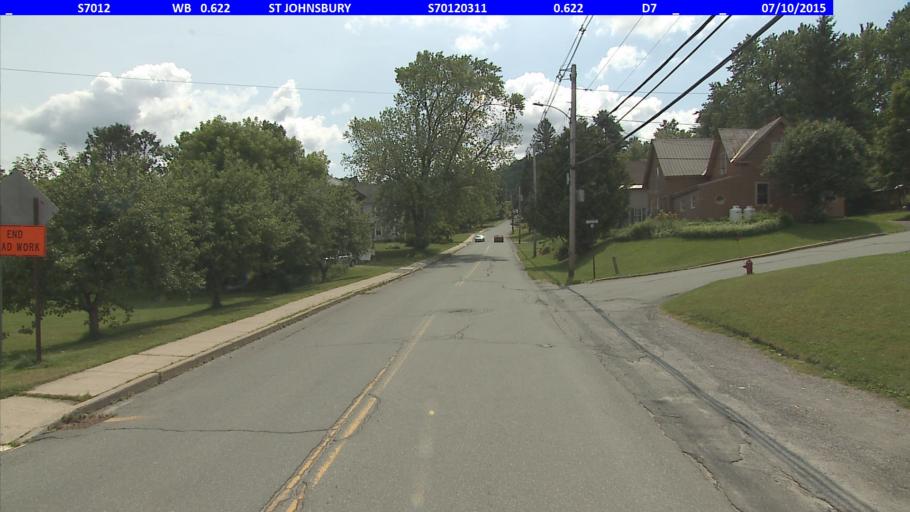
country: US
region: Vermont
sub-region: Caledonia County
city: Saint Johnsbury
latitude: 44.4203
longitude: -72.0025
